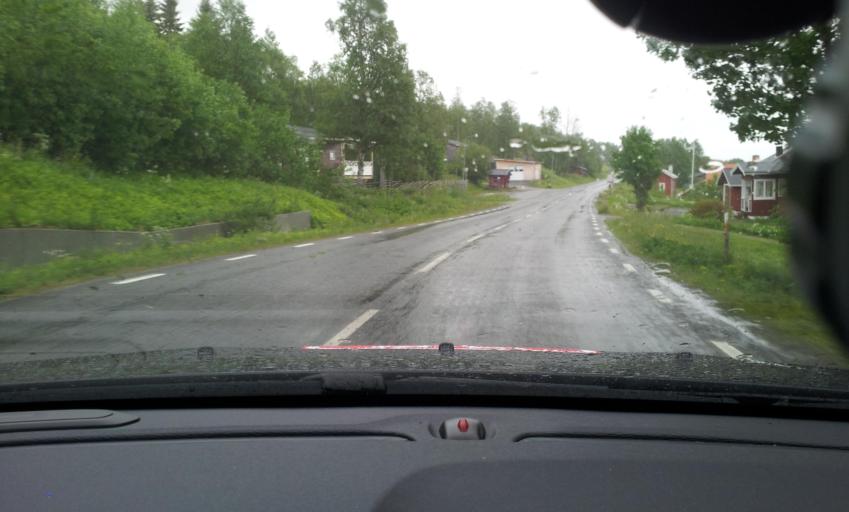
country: SE
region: Jaemtland
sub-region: Are Kommun
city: Are
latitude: 63.2171
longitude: 13.0425
